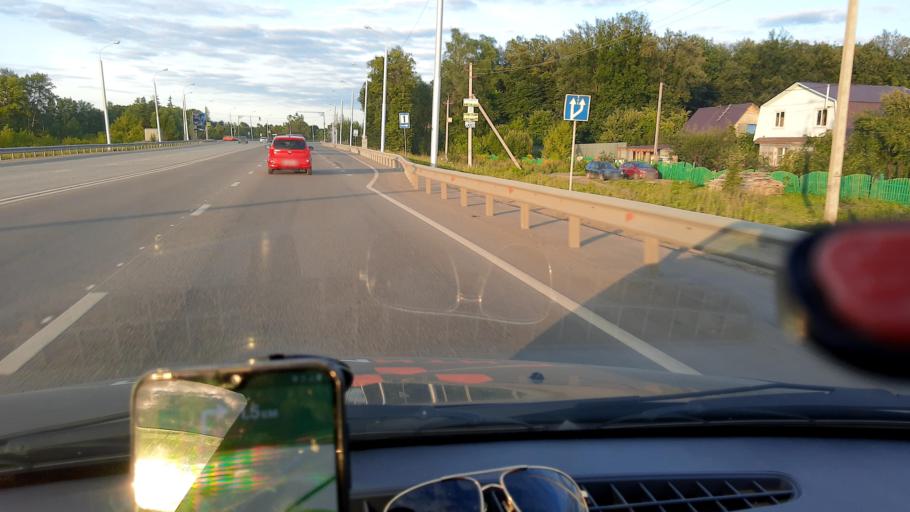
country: RU
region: Bashkortostan
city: Ufa
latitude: 54.8088
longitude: 56.1597
